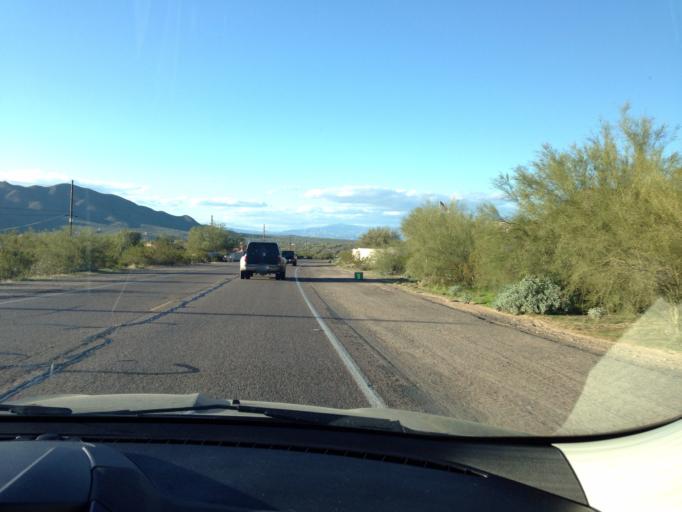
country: US
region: Arizona
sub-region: Maricopa County
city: Anthem
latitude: 33.8674
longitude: -112.0610
